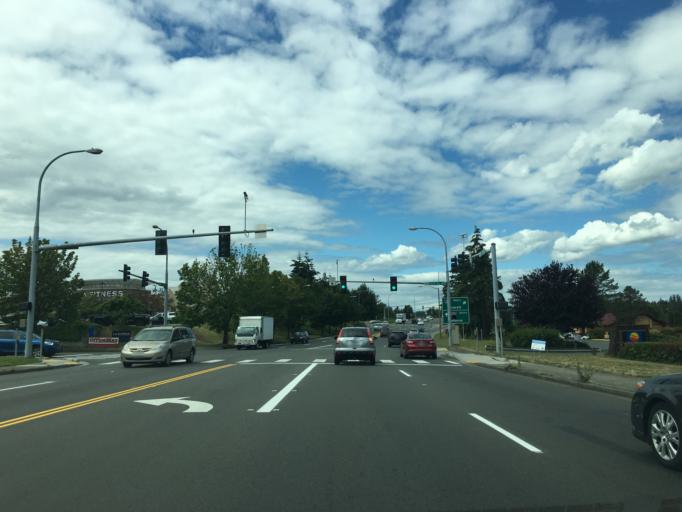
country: US
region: Washington
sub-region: King County
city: Kingsgate
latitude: 47.7089
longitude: -122.1775
